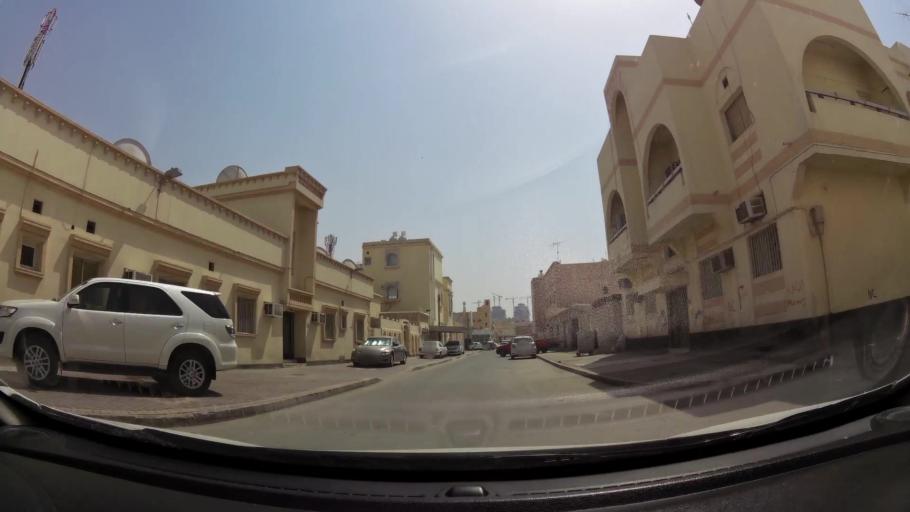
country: BH
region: Manama
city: Jidd Hafs
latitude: 26.2140
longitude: 50.4497
